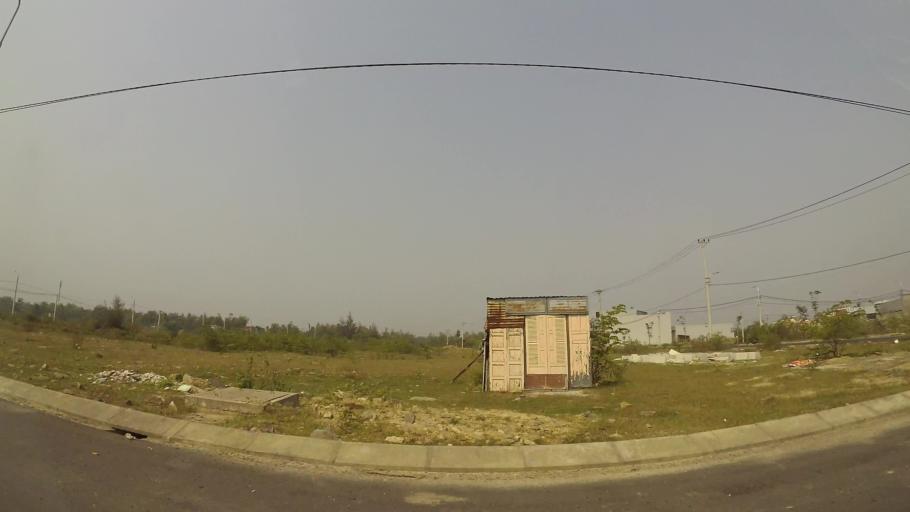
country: VN
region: Da Nang
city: Cam Le
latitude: 15.9816
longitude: 108.2273
